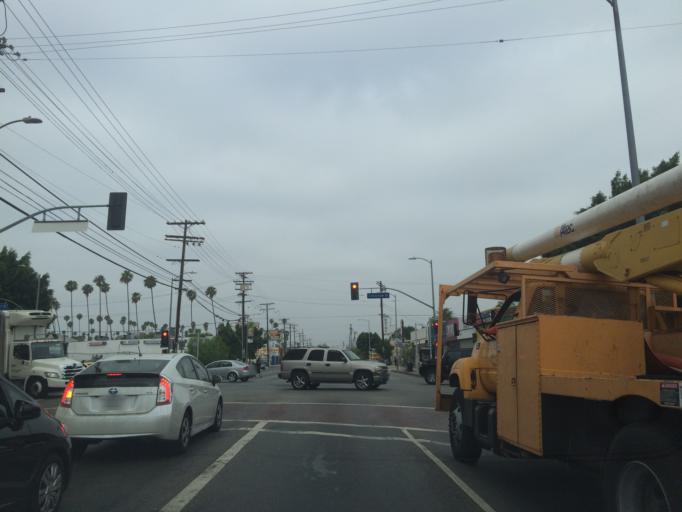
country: US
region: California
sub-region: Los Angeles County
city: Hollywood
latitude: 34.0478
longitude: -118.3264
